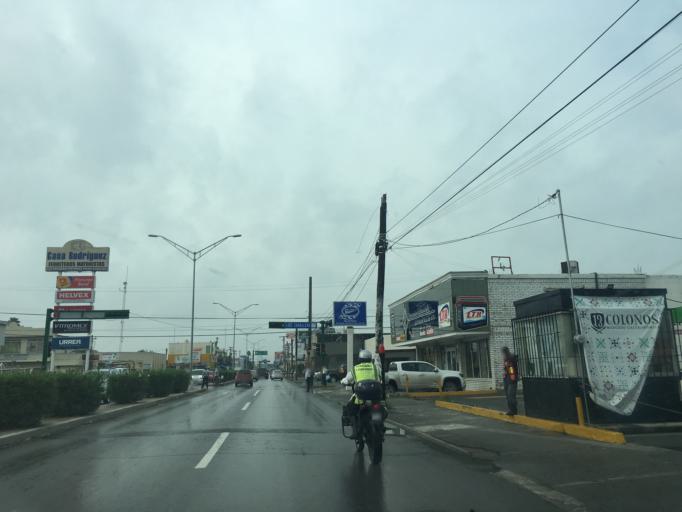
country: MX
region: Tamaulipas
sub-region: Matamoros
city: Heroica Matamoros
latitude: 25.8693
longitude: -97.5040
